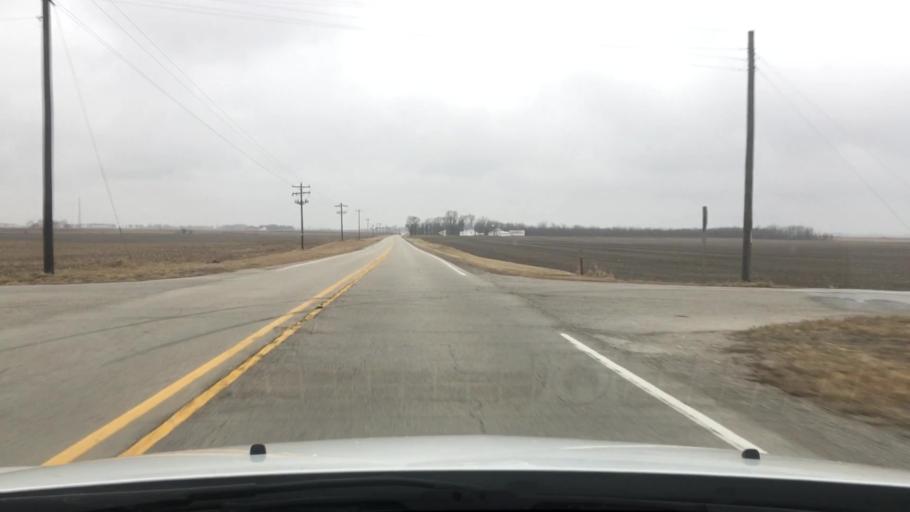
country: US
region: Illinois
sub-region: Iroquois County
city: Watseka
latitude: 40.8905
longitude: -87.7116
